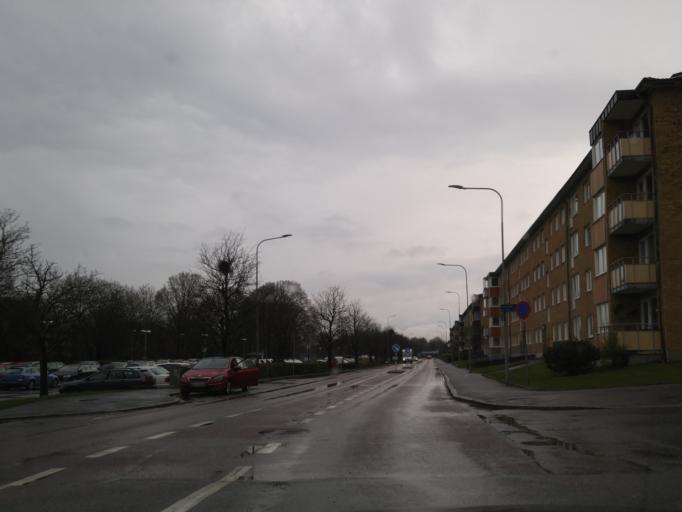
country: SE
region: Vaestra Goetaland
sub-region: Goteborg
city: Majorna
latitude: 57.6639
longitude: 11.9349
